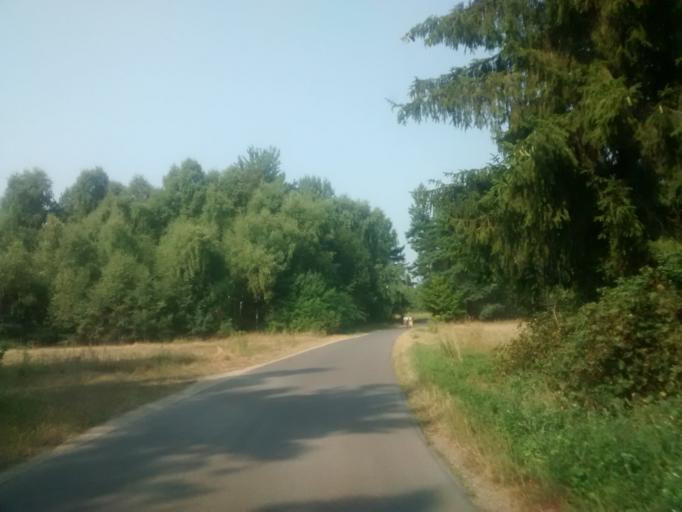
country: PL
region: Silesian Voivodeship
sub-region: Powiat zawiercianski
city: Wlodowice
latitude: 50.6113
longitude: 19.4818
